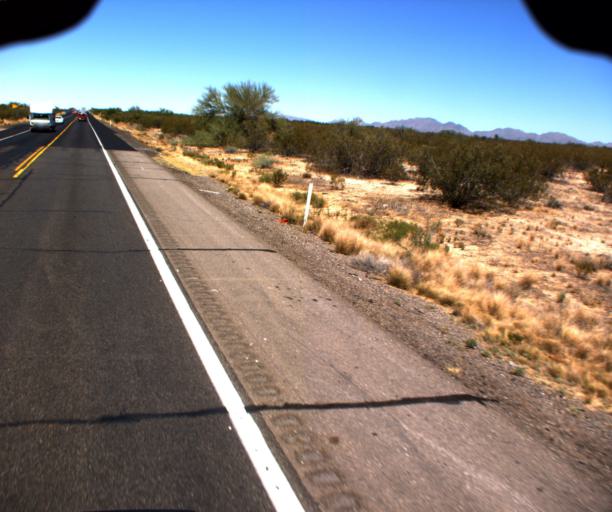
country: US
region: Arizona
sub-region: Yavapai County
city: Congress
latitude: 34.0519
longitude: -112.8478
